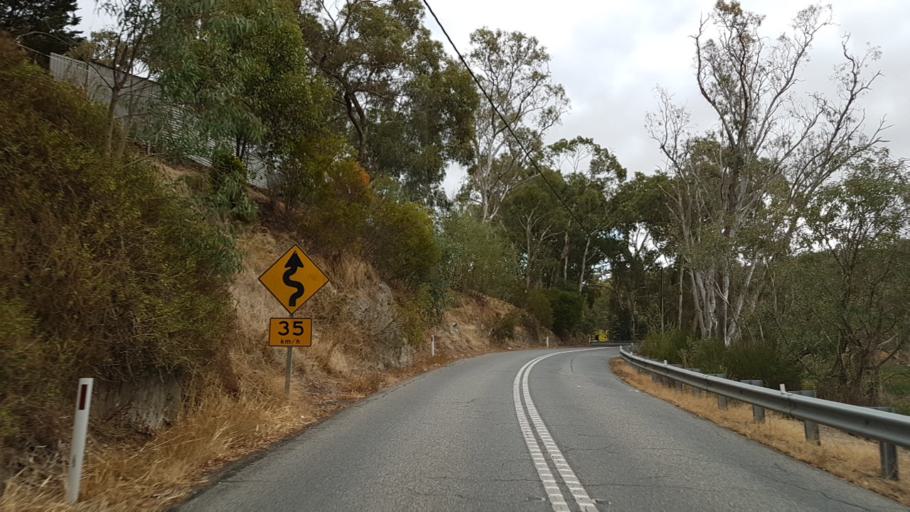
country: AU
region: South Australia
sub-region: Adelaide Hills
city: Gumeracha
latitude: -34.8398
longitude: 138.8147
